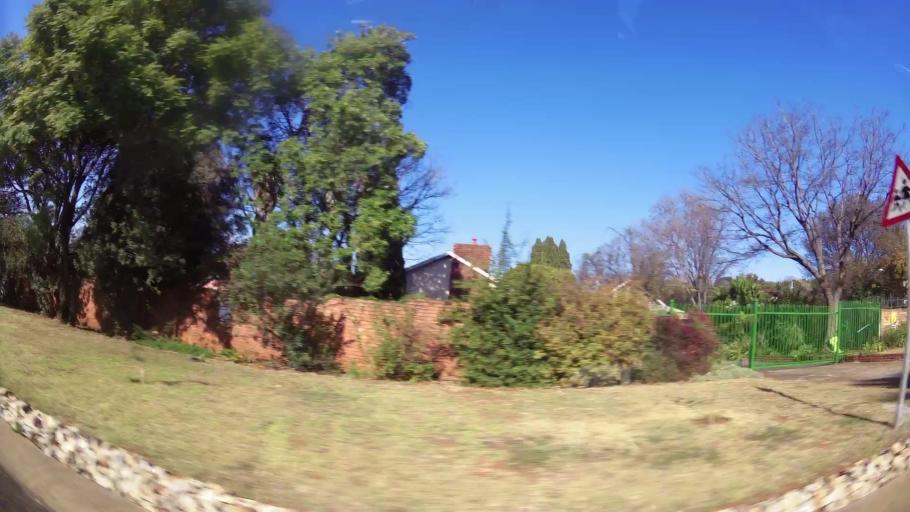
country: ZA
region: Gauteng
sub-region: City of Tshwane Metropolitan Municipality
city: Centurion
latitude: -25.8482
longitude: 28.1709
